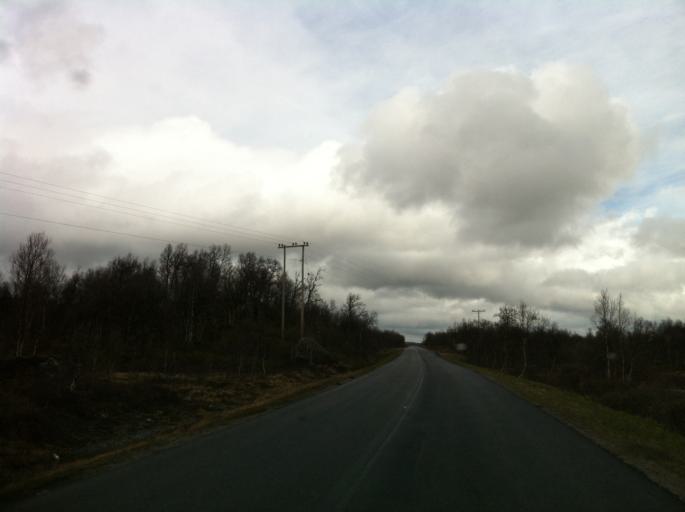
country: NO
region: Sor-Trondelag
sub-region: Tydal
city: Aas
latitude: 62.6355
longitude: 11.9715
